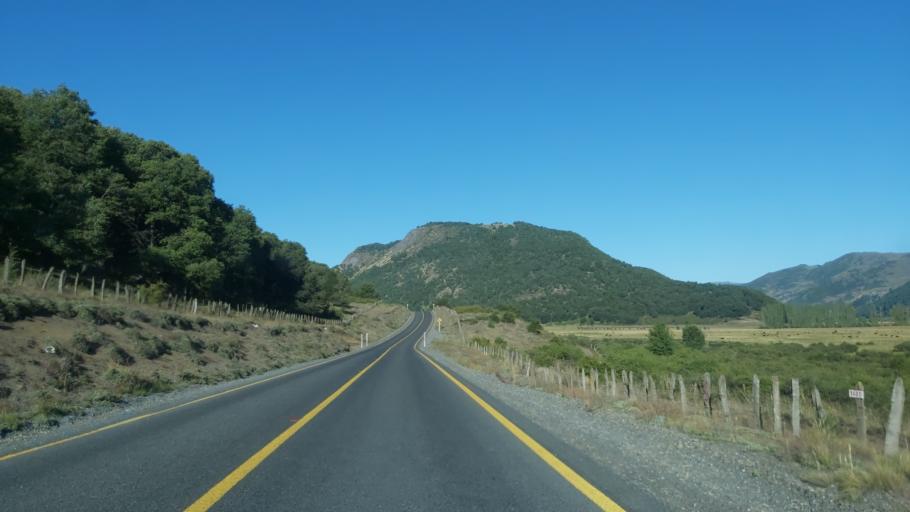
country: AR
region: Neuquen
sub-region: Departamento de Loncopue
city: Loncopue
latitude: -38.4451
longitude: -71.3499
